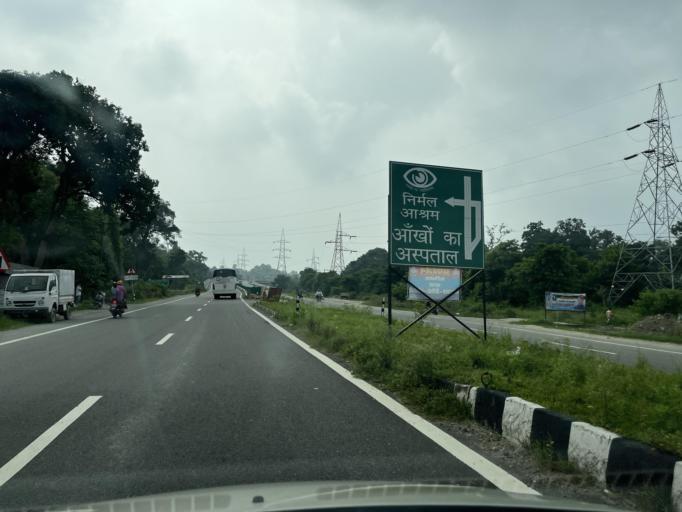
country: IN
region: Uttarakhand
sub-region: Dehradun
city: Raiwala
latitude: 30.0722
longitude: 78.2029
